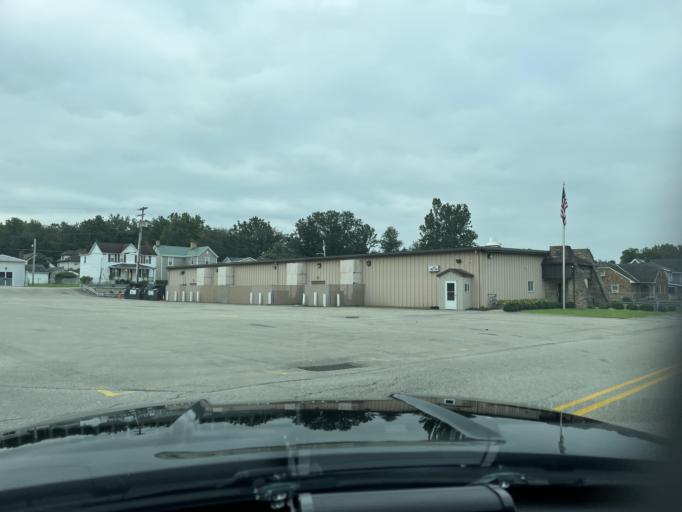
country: US
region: Pennsylvania
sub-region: Fayette County
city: Hopwood
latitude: 39.8756
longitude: -79.7018
